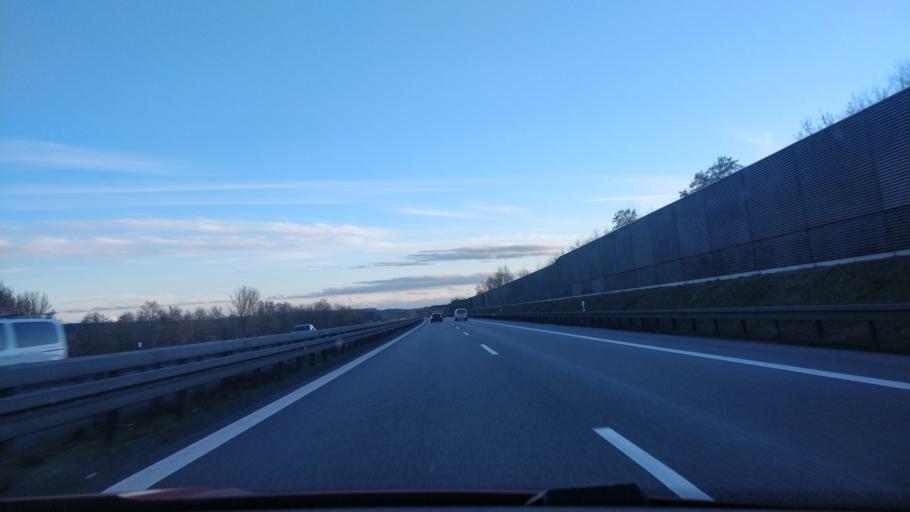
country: DE
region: Bavaria
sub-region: Upper Palatinate
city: Pirk
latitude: 49.6381
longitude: 12.1475
